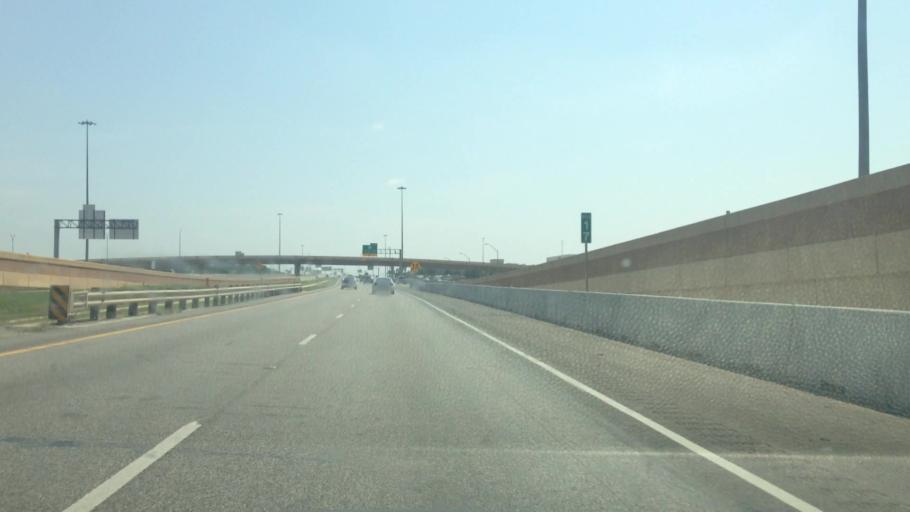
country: US
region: Texas
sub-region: Tarrant County
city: Blue Mound
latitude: 32.8392
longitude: -97.3048
